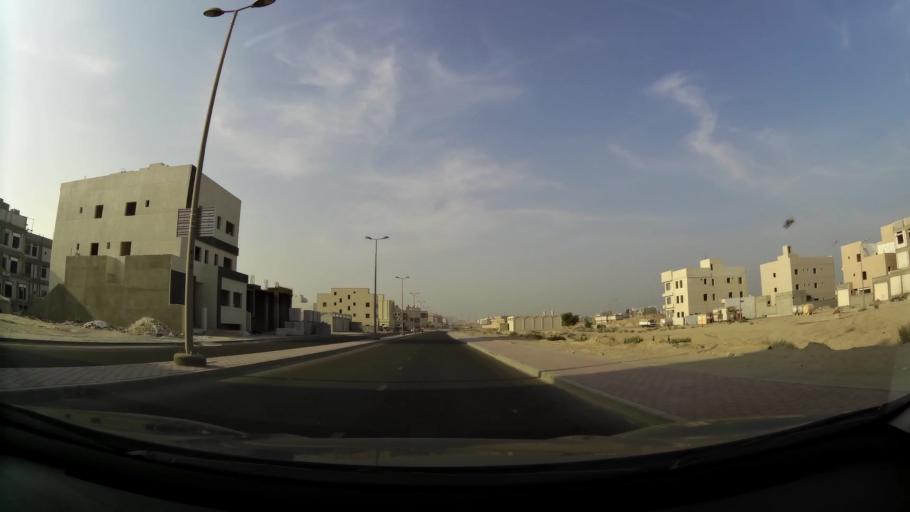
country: KW
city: Al Funaytis
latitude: 29.2230
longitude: 48.0920
